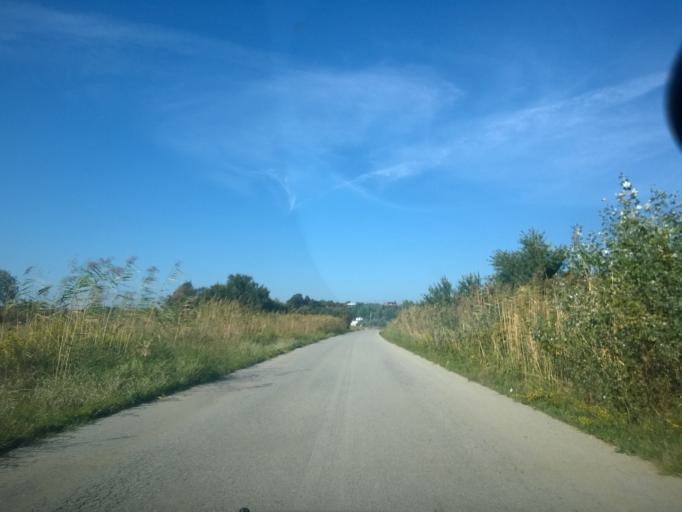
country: GR
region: Central Macedonia
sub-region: Nomos Chalkidikis
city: Nea Kallikrateia
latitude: 40.3286
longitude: 23.0234
